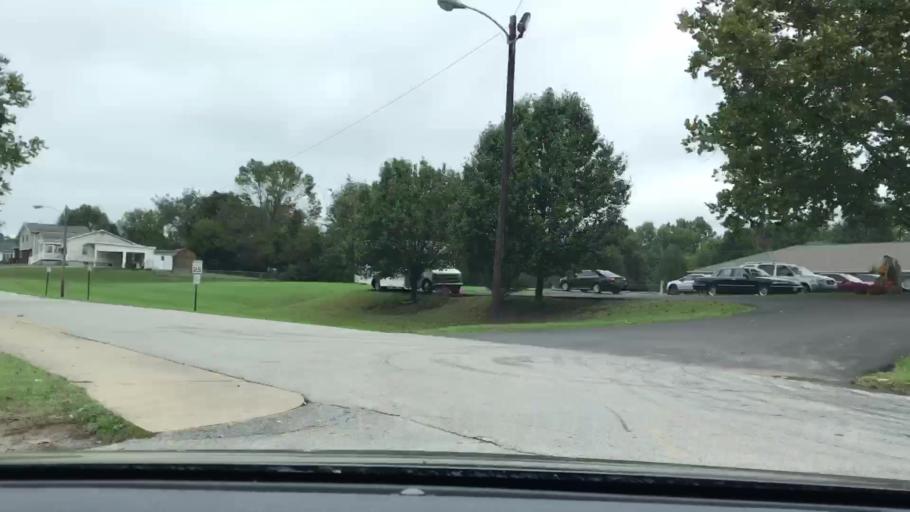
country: US
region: Kentucky
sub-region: Pulaski County
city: Somerset
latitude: 37.0839
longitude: -84.5971
